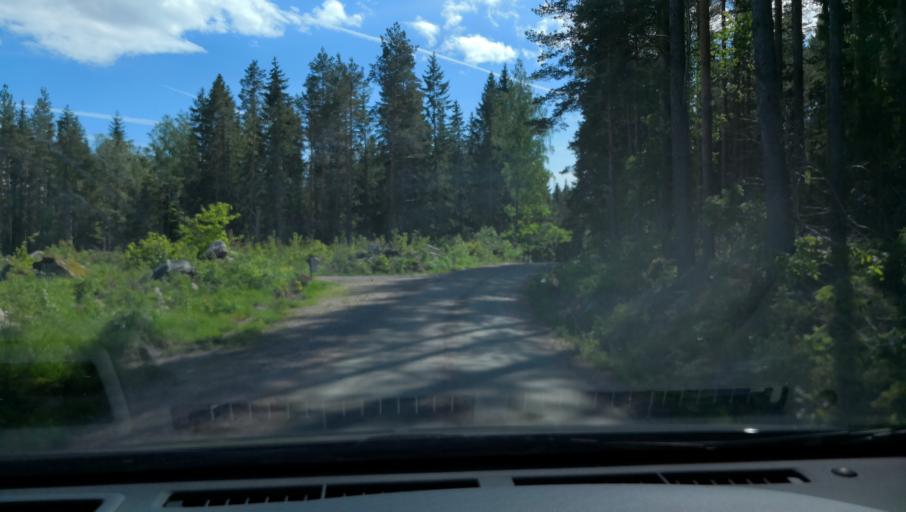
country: SE
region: Vaestmanland
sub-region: Arboga Kommun
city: Tyringe
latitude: 59.3145
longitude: 15.9946
